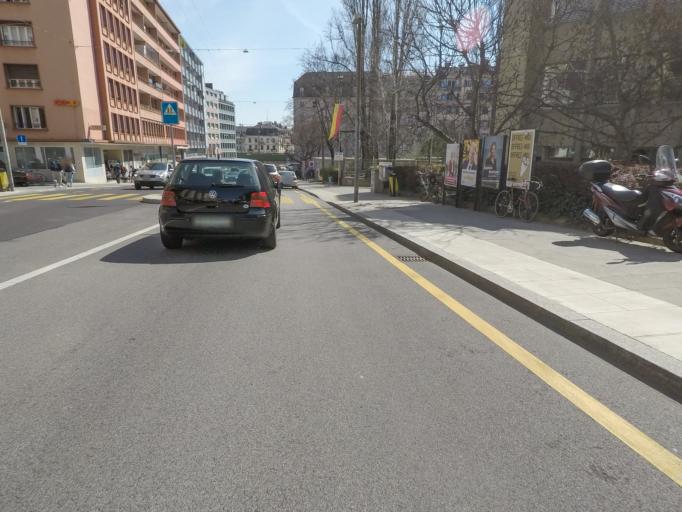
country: CH
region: Geneva
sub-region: Geneva
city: Geneve
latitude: 46.2079
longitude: 6.1366
